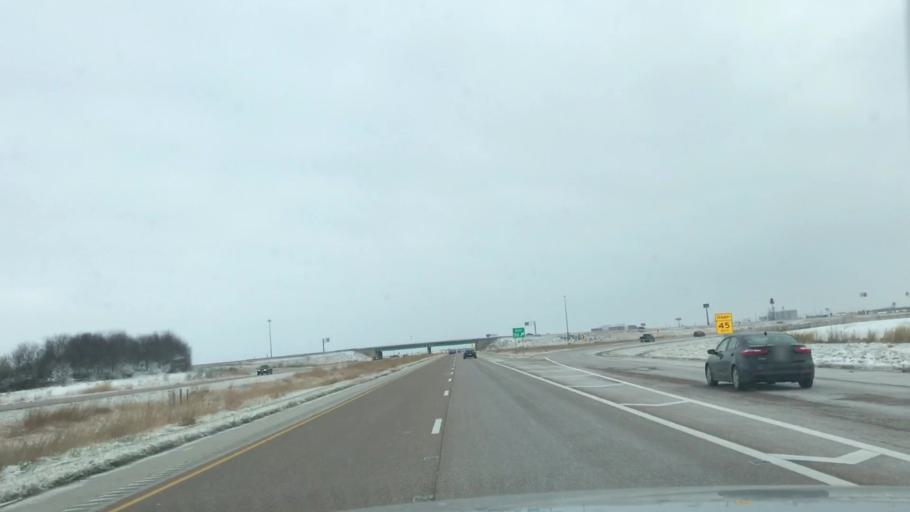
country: US
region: Illinois
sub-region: Montgomery County
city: Litchfield
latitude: 39.1712
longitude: -89.6838
